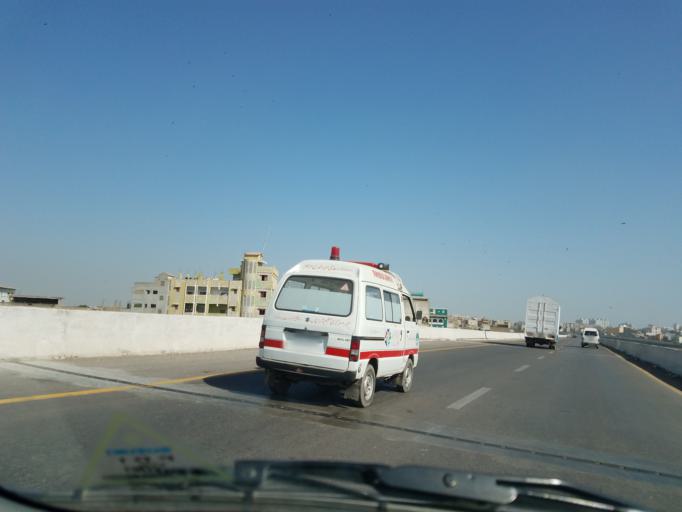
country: PK
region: Sindh
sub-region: Karachi District
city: Karachi
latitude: 24.8821
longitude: 67.0055
